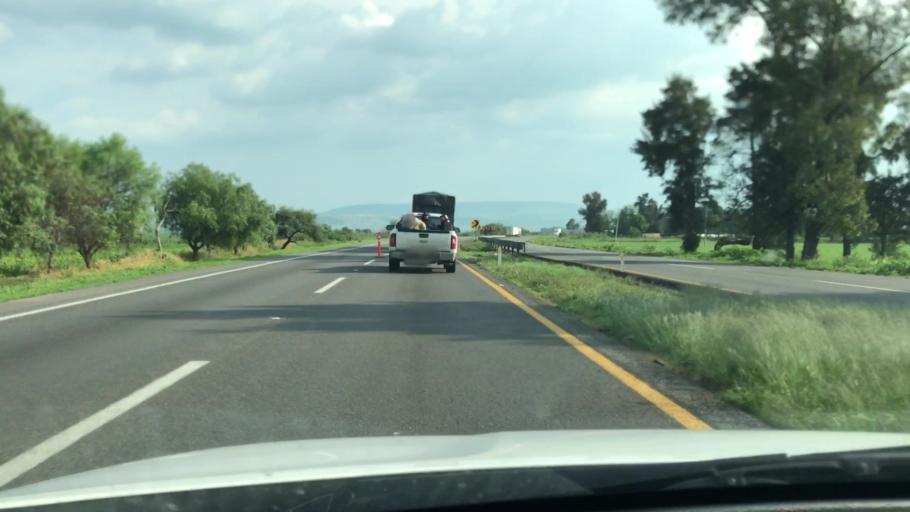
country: MX
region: Guanajuato
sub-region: Irapuato
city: San Ignacio de Rivera (Ojo de Agua)
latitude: 20.5196
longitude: -101.4643
